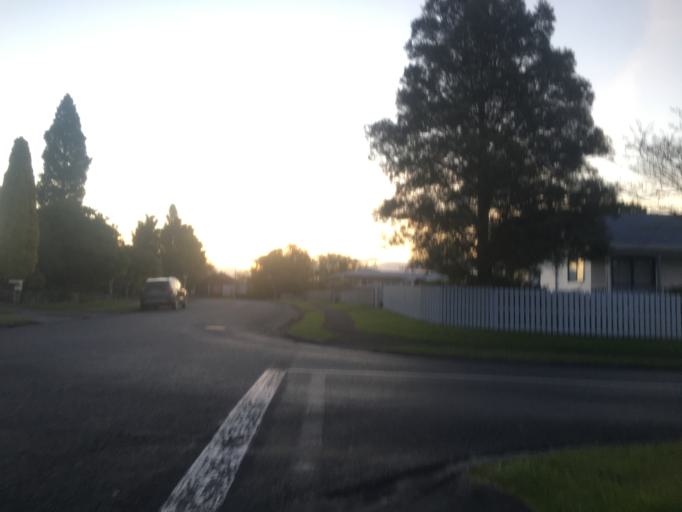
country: NZ
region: Waikato
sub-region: Waipa District
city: Cambridge
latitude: -38.0058
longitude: 175.3371
